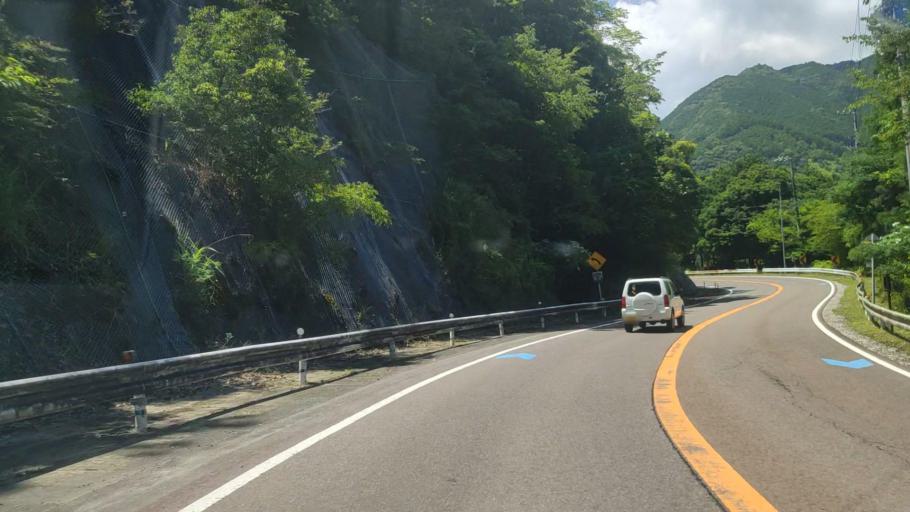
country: JP
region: Mie
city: Owase
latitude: 34.1024
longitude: 136.2044
